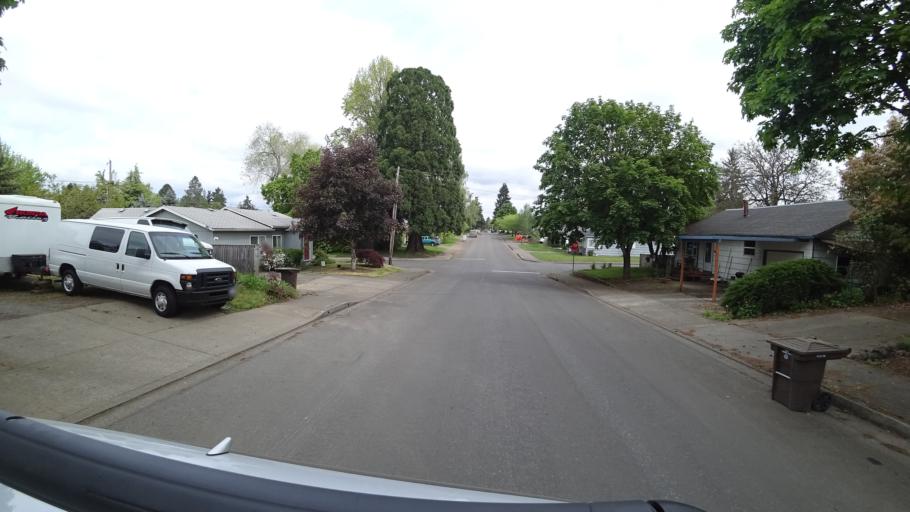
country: US
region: Oregon
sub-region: Washington County
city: Hillsboro
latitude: 45.5237
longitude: -122.9963
